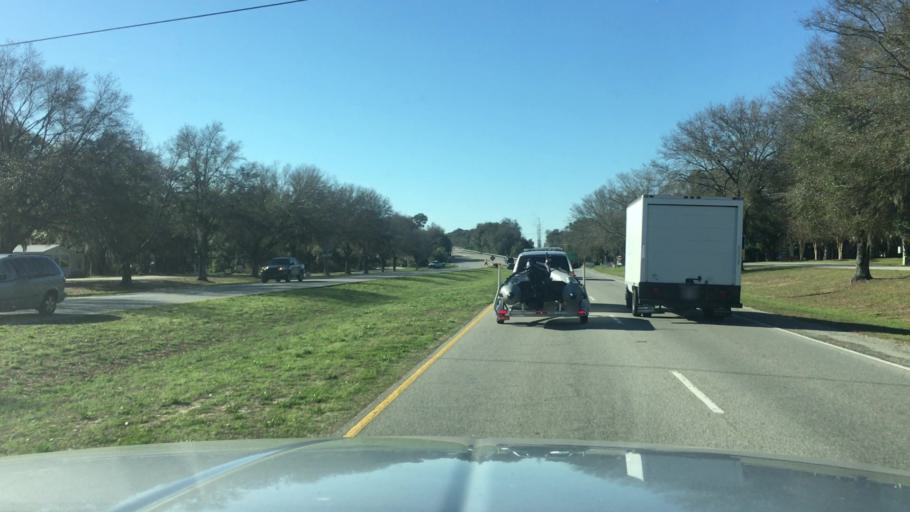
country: US
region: North Carolina
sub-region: New Hanover County
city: Sea Breeze
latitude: 34.0629
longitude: -77.8989
